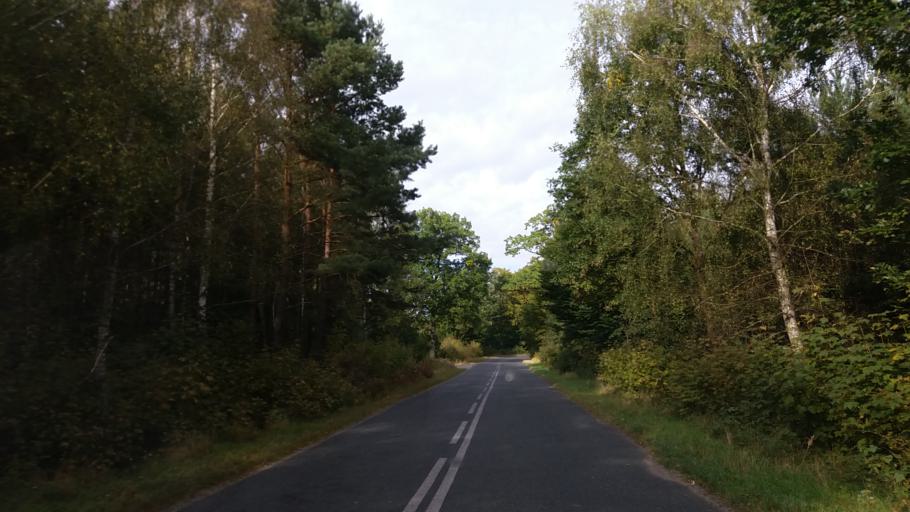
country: PL
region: West Pomeranian Voivodeship
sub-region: Powiat choszczenski
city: Krzecin
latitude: 53.0109
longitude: 15.5021
